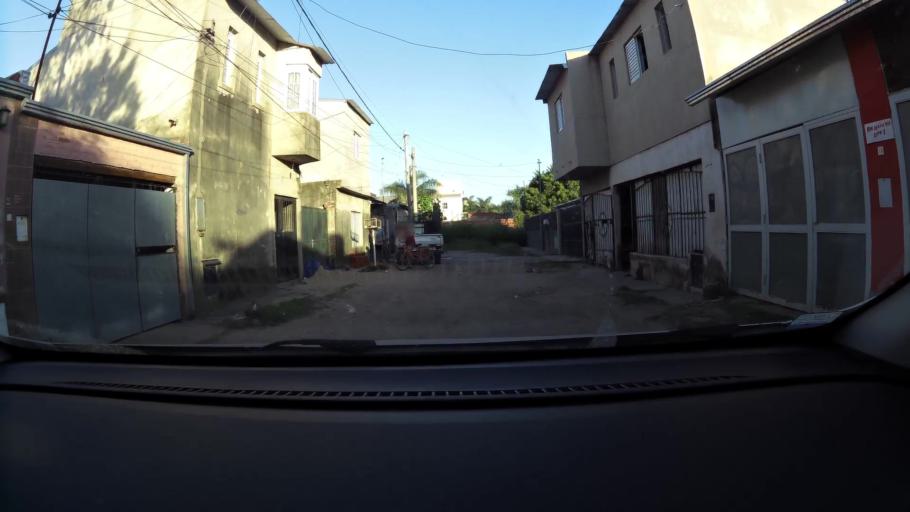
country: AR
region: Santa Fe
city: Santa Fe de la Vera Cruz
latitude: -31.5959
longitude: -60.6876
